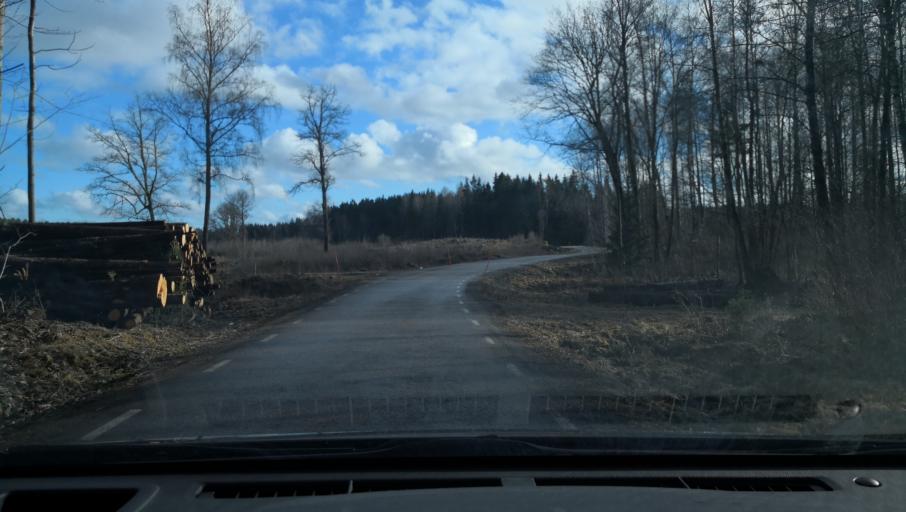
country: SE
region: Vaestmanland
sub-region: Arboga Kommun
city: Arboga
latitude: 59.3219
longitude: 15.7583
